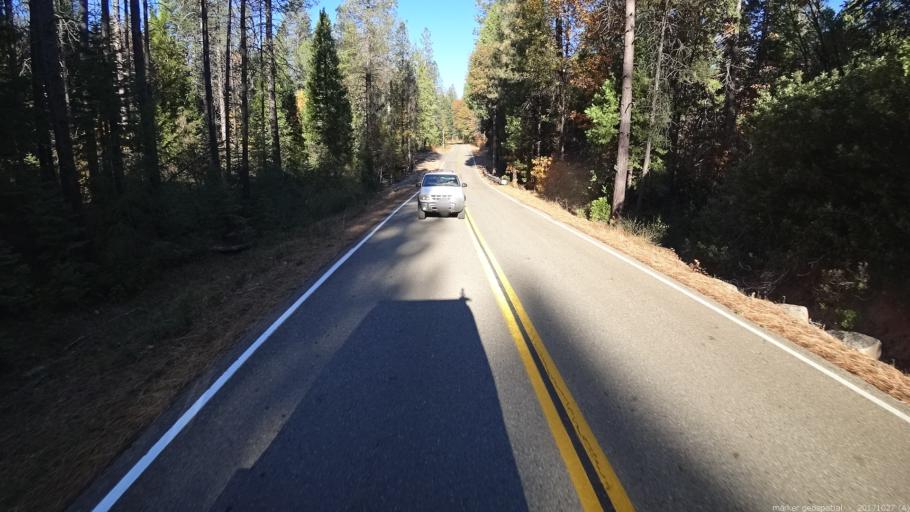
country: US
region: California
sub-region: Shasta County
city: Burney
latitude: 40.9324
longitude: -121.9459
